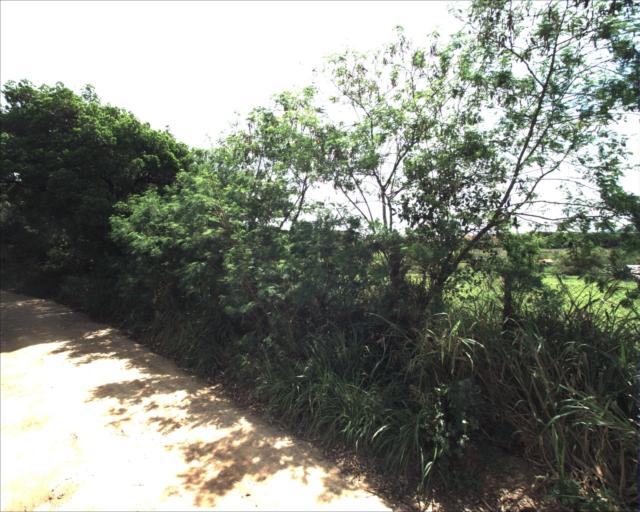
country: BR
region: Sao Paulo
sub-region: Aracoiaba Da Serra
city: Aracoiaba da Serra
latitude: -23.5557
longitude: -47.5515
